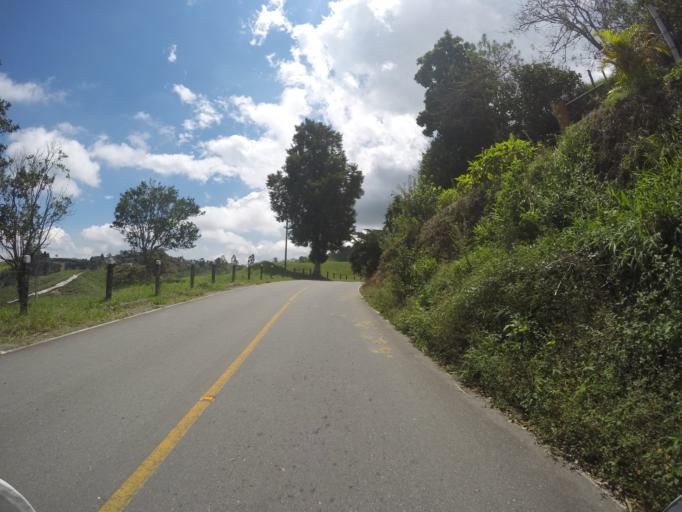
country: CO
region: Quindio
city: Filandia
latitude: 4.6545
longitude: -75.6761
